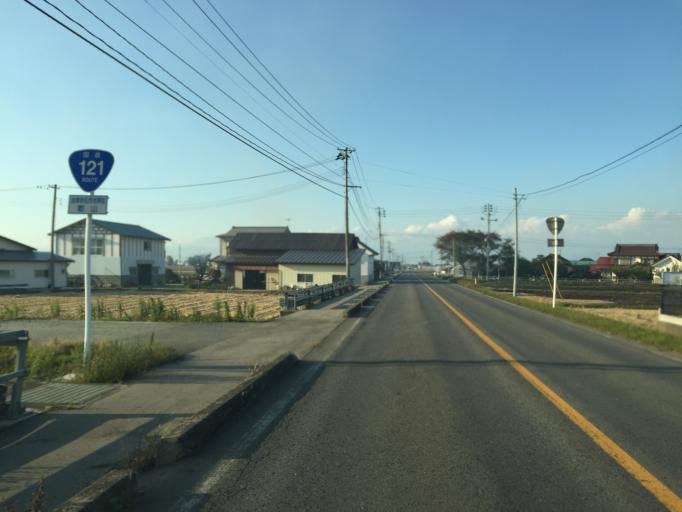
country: JP
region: Fukushima
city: Kitakata
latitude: 37.5464
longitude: 139.9117
